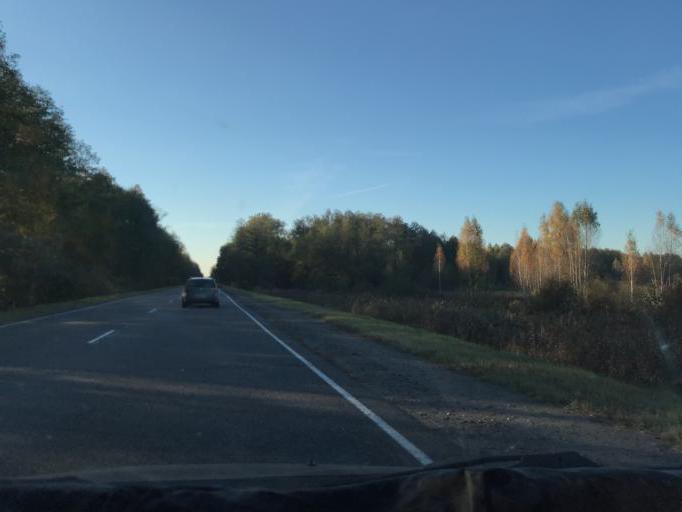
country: BY
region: Gomel
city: Pyetrykaw
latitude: 52.2642
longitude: 28.3096
